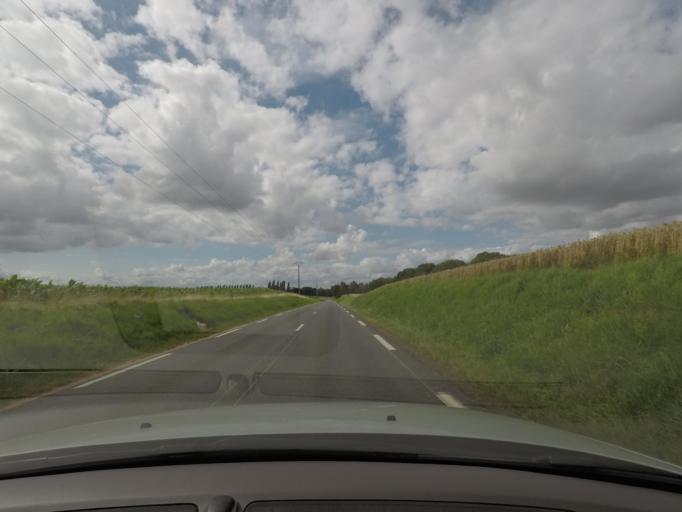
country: FR
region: Haute-Normandie
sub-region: Departement de l'Eure
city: Les Andelys
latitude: 49.2340
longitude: 1.4310
